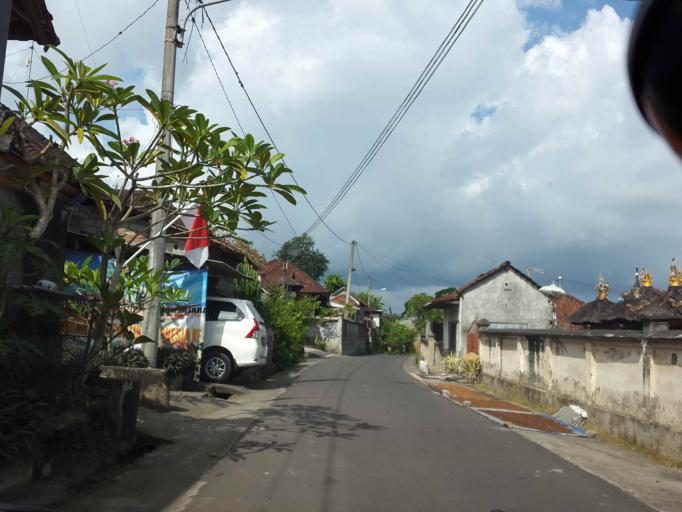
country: ID
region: Bali
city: Banjar Kelodan
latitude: -8.5181
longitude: 115.3722
